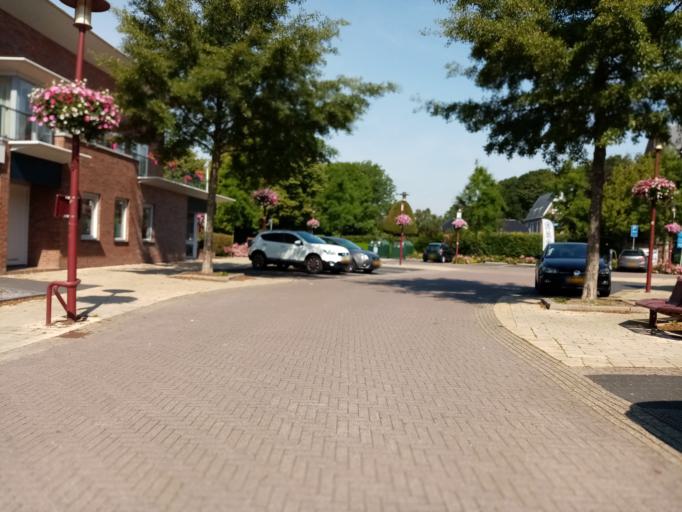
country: NL
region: South Holland
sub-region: Gemeente Kaag en Braassem
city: Leimuiden
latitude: 52.1928
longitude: 4.7118
